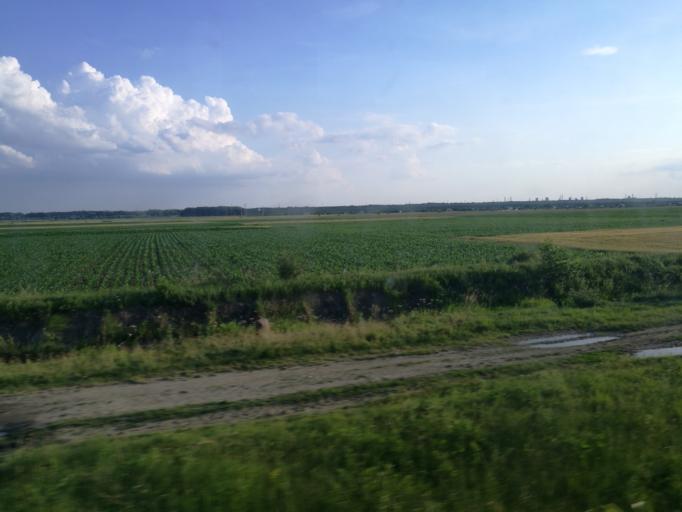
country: RO
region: Arges
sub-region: Comuna Calinesti
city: Vranesti
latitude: 44.8258
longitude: 25.0109
